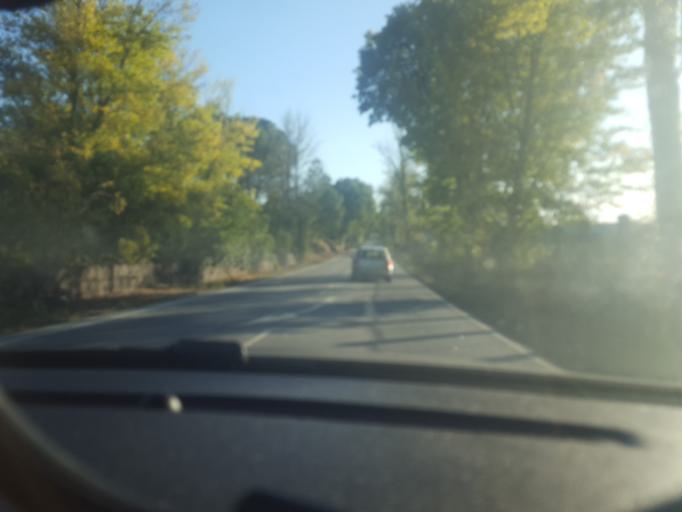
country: PT
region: Viseu
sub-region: Nelas
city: Nelas
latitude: 40.4917
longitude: -7.9029
